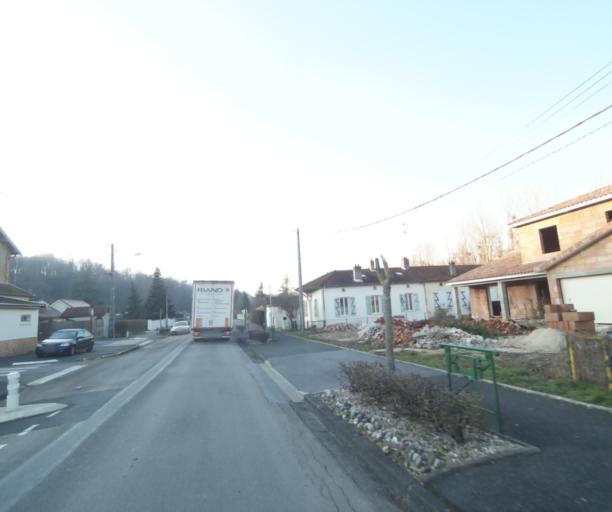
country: FR
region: Champagne-Ardenne
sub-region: Departement de la Haute-Marne
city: Bienville
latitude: 48.5459
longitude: 5.0833
